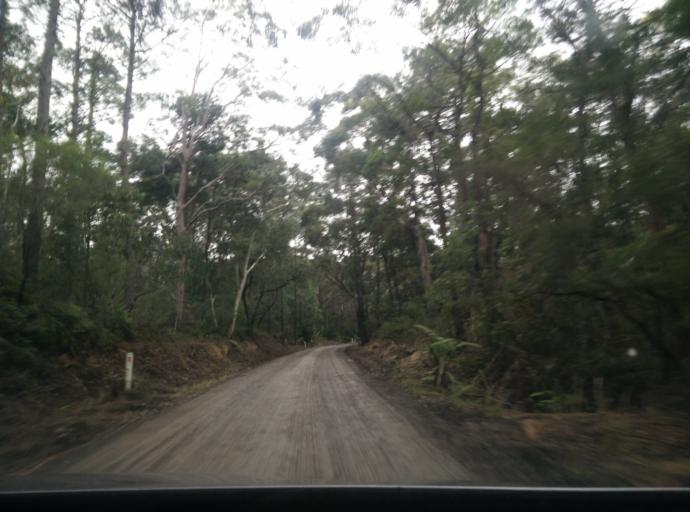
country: AU
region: New South Wales
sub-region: Gosford Shire
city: Narara
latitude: -33.3692
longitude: 151.3231
